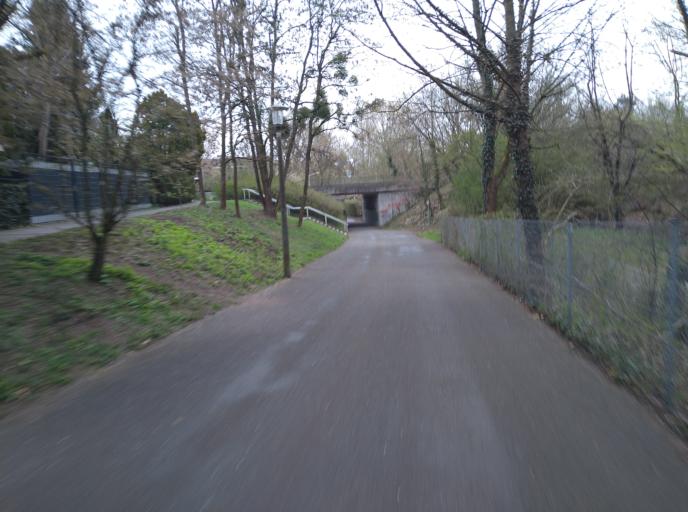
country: DE
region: Bavaria
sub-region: Regierungsbezirk Mittelfranken
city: Nuernberg
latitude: 49.4464
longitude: 11.1158
